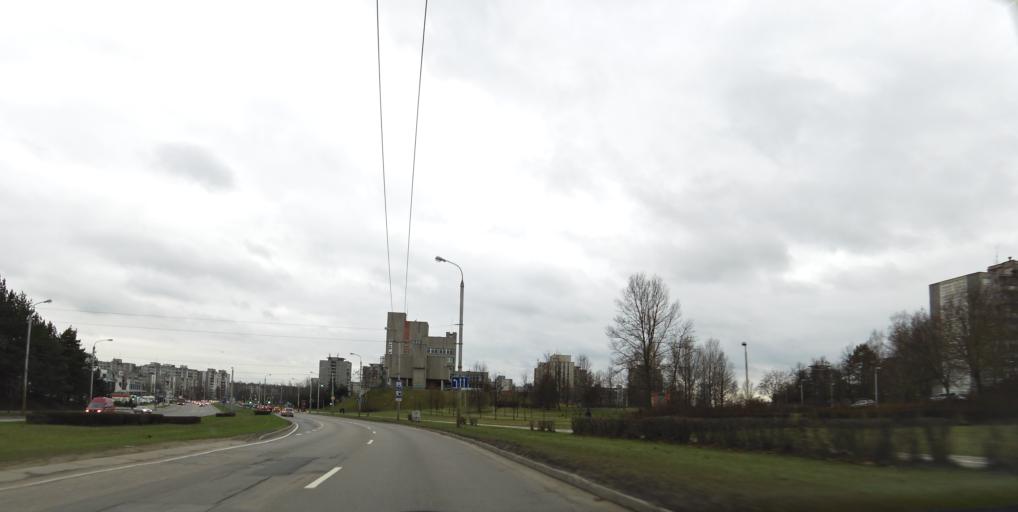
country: LT
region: Vilnius County
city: Justiniskes
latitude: 54.7109
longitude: 25.2262
